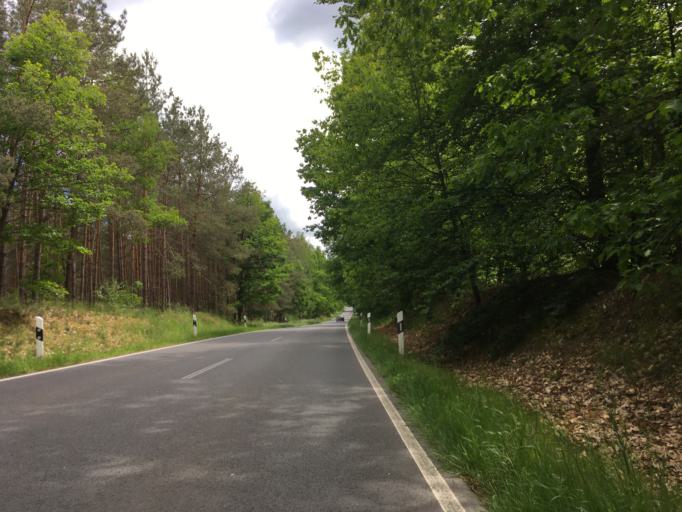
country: DE
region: Brandenburg
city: Falkenberg
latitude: 52.7635
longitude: 13.9677
